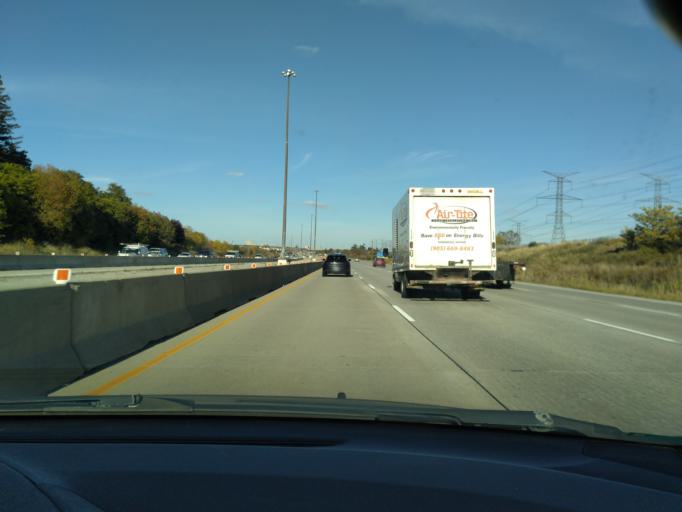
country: CA
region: Ontario
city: Brampton
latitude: 43.6258
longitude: -79.7525
